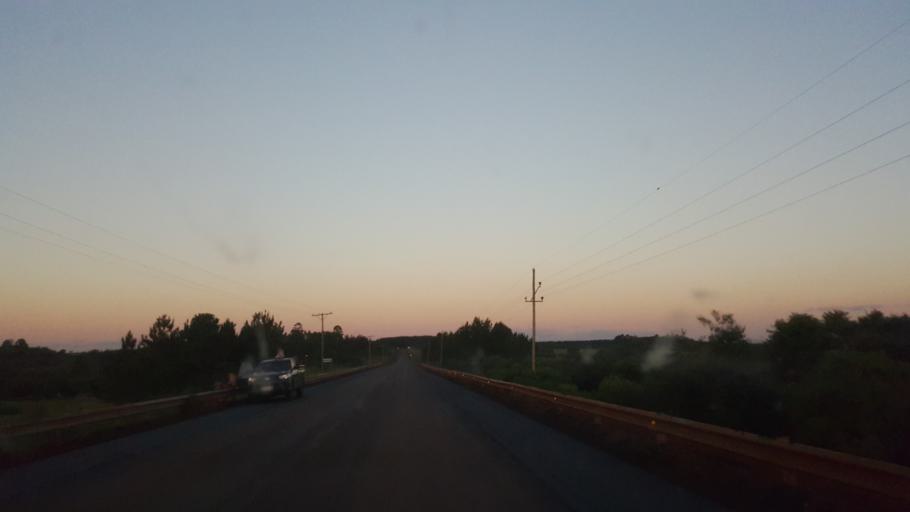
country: AR
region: Corrientes
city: Garruchos
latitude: -28.2330
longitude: -55.8134
